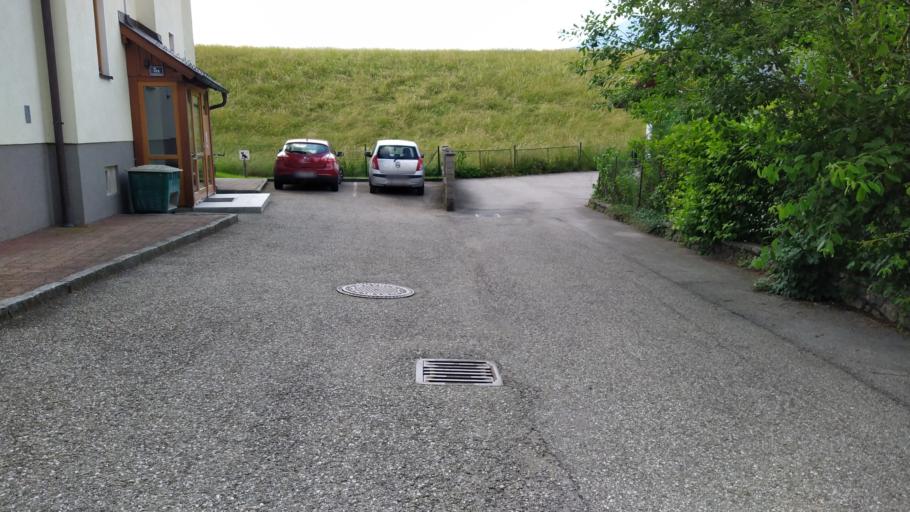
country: AT
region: Upper Austria
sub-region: Politischer Bezirk Gmunden
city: Bad Ischl
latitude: 47.7050
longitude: 13.6314
